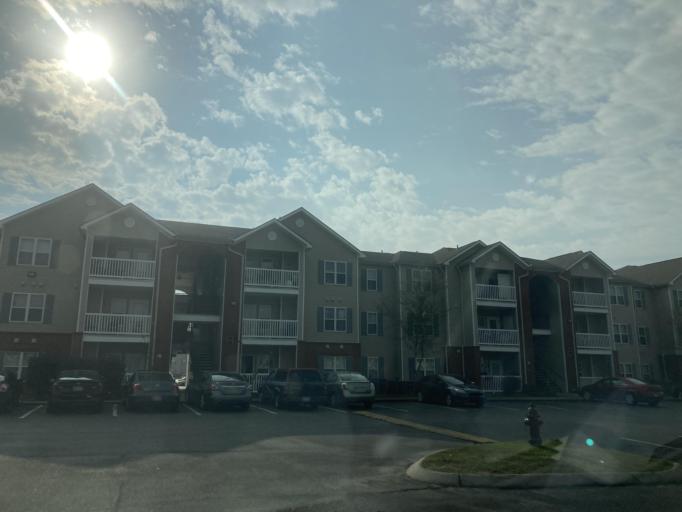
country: US
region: Mississippi
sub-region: Harrison County
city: Gulfport
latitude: 30.3700
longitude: -89.1210
